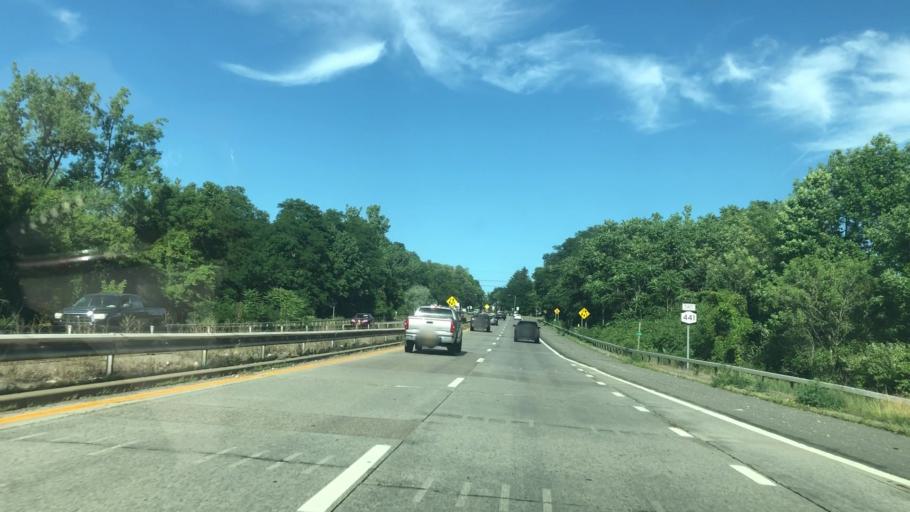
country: US
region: New York
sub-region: Monroe County
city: East Rochester
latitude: 43.1280
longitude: -77.4885
